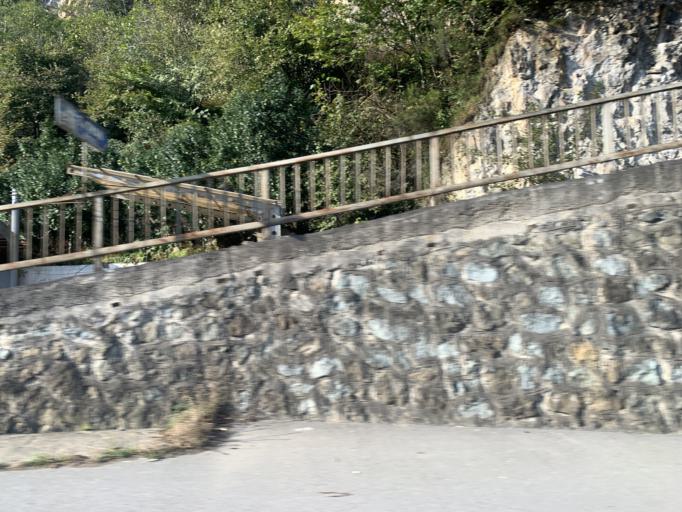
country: TR
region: Trabzon
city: Dernekpazari
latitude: 40.8365
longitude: 40.2731
